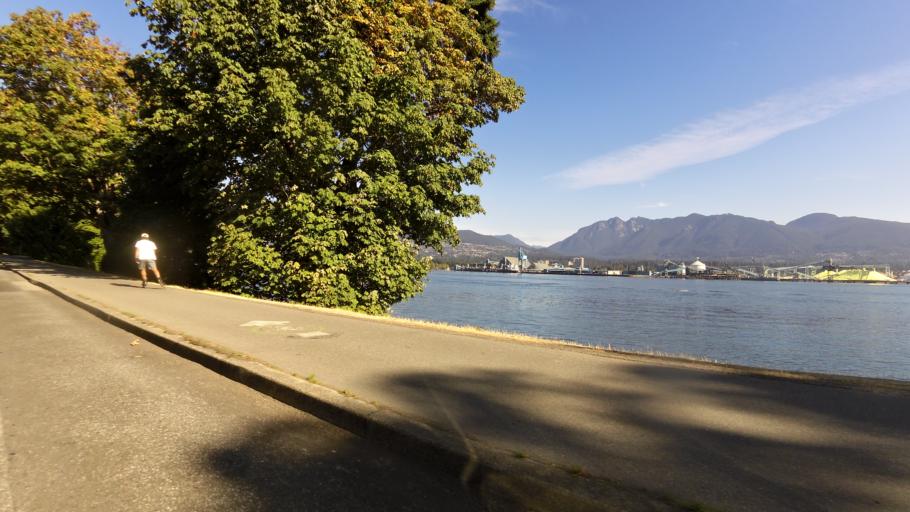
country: CA
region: British Columbia
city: West End
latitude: 49.3004
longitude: -123.1231
